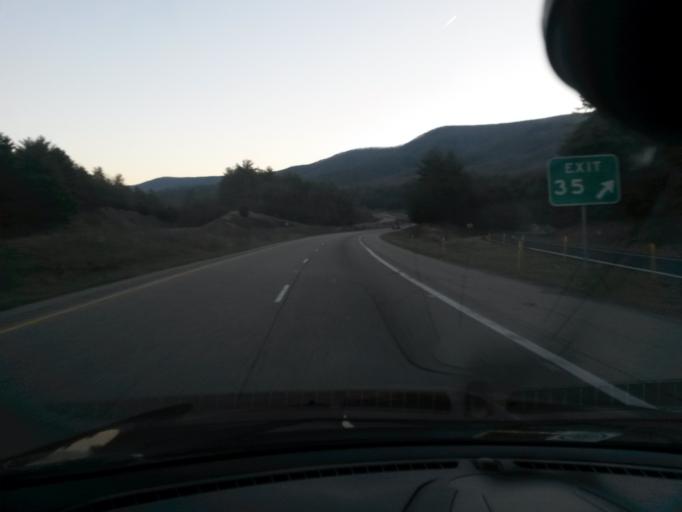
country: US
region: Virginia
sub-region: Alleghany County
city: Clifton Forge
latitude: 37.8129
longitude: -79.6808
